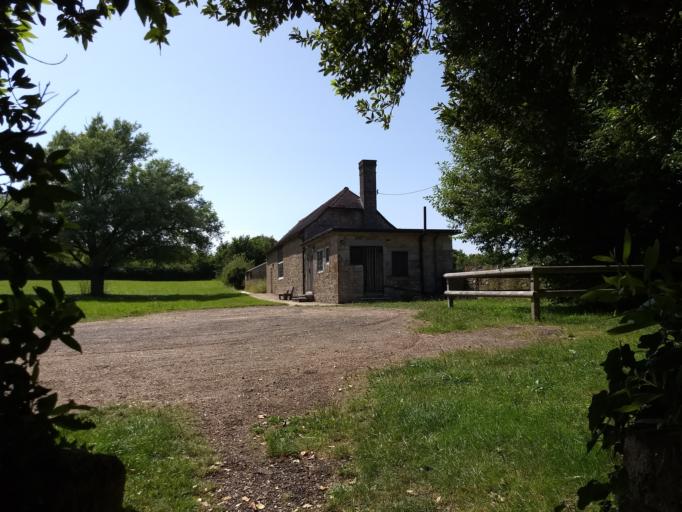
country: GB
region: England
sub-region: Isle of Wight
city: Shalfleet
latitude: 50.7014
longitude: -1.4161
